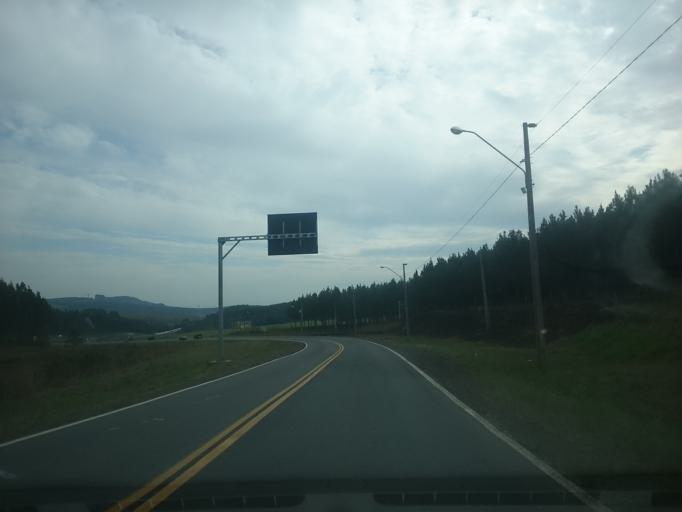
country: BR
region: Santa Catarina
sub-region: Lages
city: Lages
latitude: -27.7530
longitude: -50.3318
